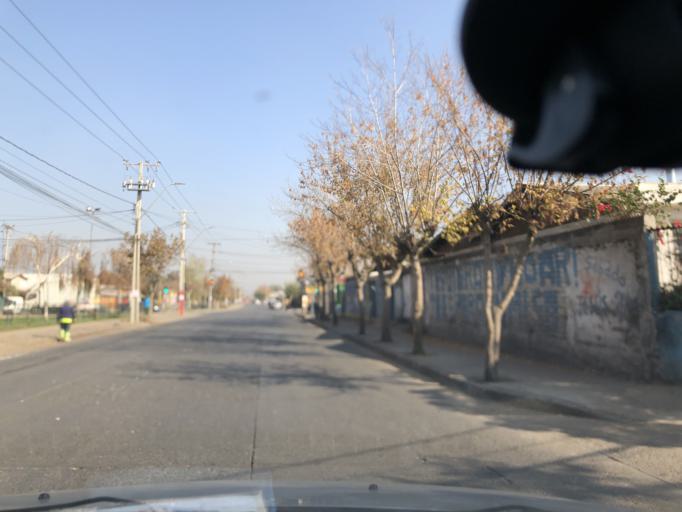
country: CL
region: Santiago Metropolitan
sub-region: Provincia de Cordillera
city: Puente Alto
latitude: -33.6153
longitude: -70.5857
